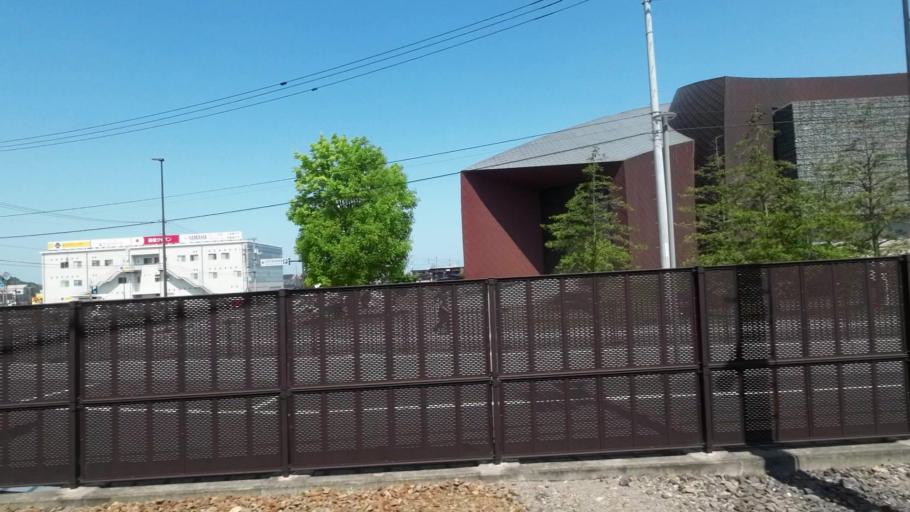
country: JP
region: Ehime
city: Niihama
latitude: 33.9488
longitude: 133.2954
